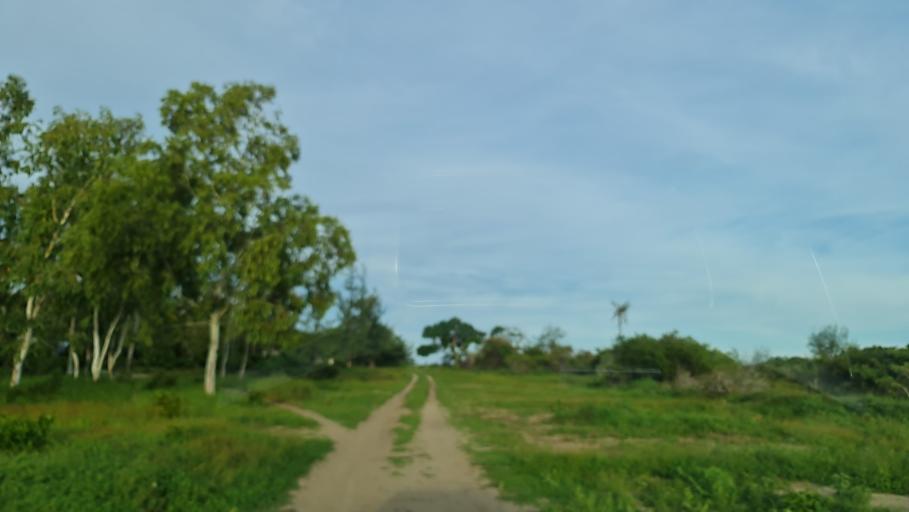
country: MZ
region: Nampula
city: Nacala
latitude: -14.7780
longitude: 40.8205
